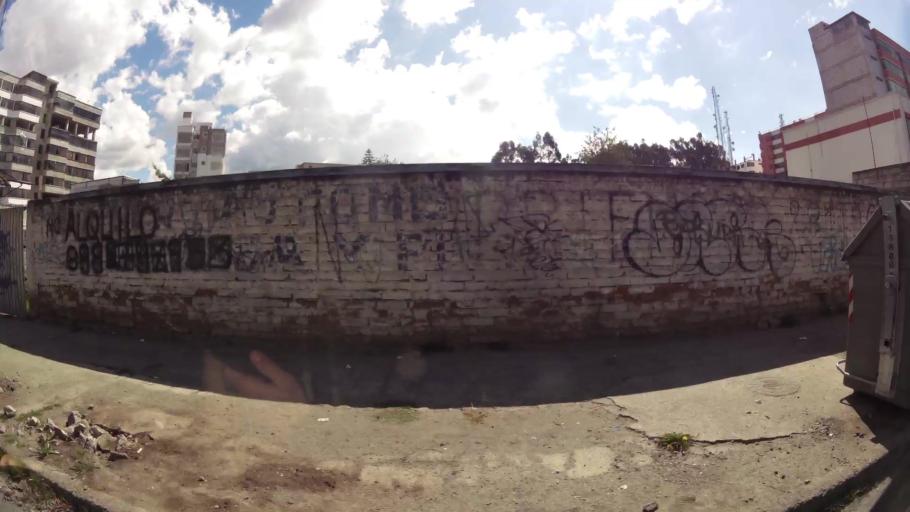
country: EC
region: Pichincha
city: Quito
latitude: -0.1223
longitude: -78.4717
